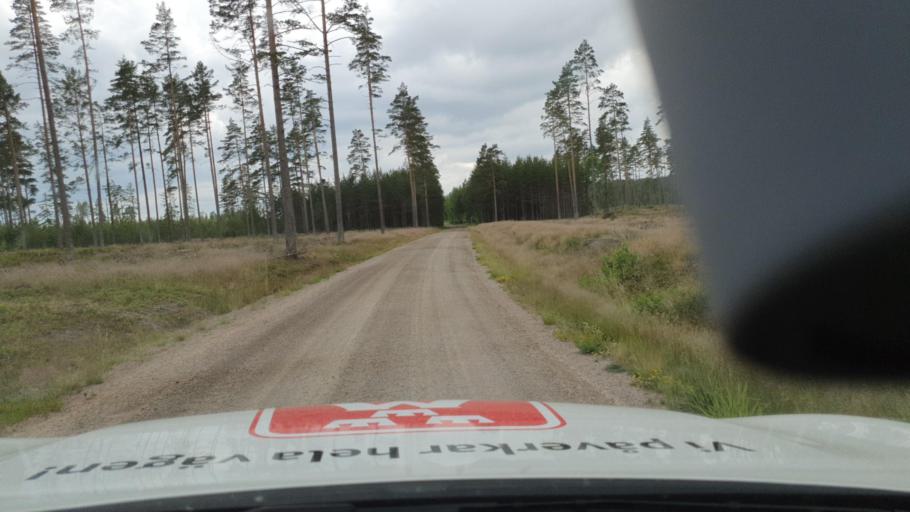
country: SE
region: Vaestra Goetaland
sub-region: Tidaholms Kommun
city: Olofstorp
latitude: 58.1868
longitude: 14.1107
